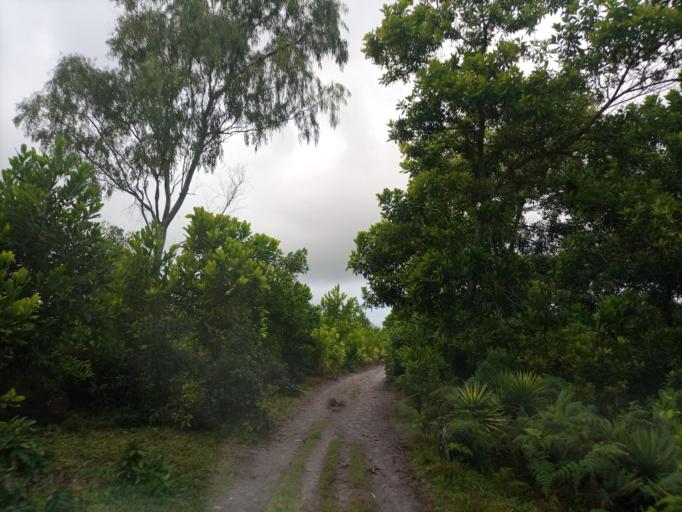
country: MG
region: Anosy
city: Fort Dauphin
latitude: -24.6464
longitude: 47.2031
